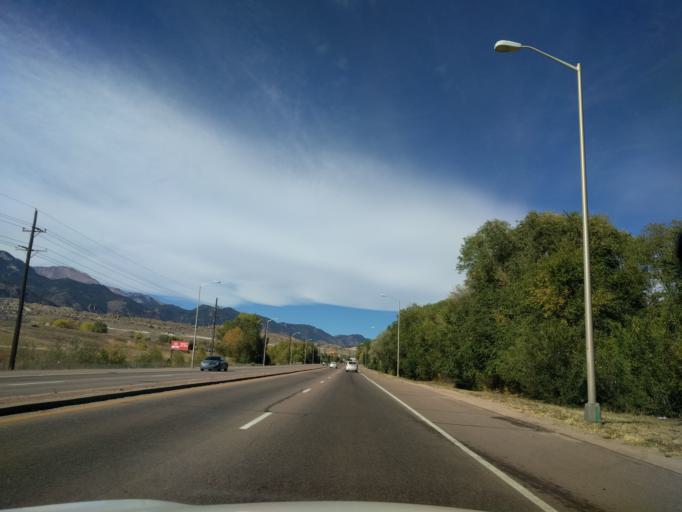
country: US
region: Colorado
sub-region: El Paso County
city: Colorado Springs
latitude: 38.8371
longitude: -104.8523
